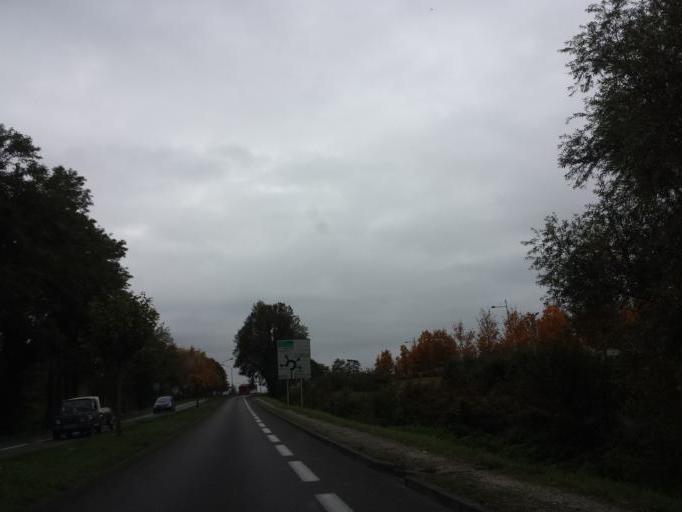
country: FR
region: Poitou-Charentes
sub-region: Departement de la Charente
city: La Couronne
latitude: 45.6254
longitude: 0.1139
